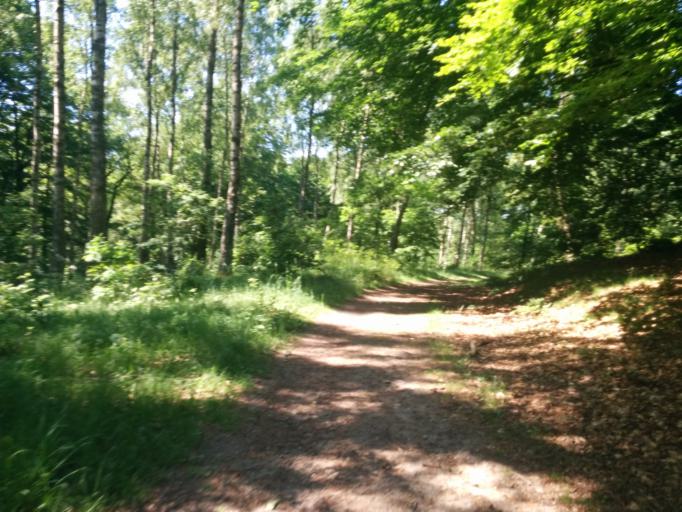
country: SE
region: Skane
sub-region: Lunds Kommun
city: Genarp
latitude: 55.5855
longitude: 13.3868
